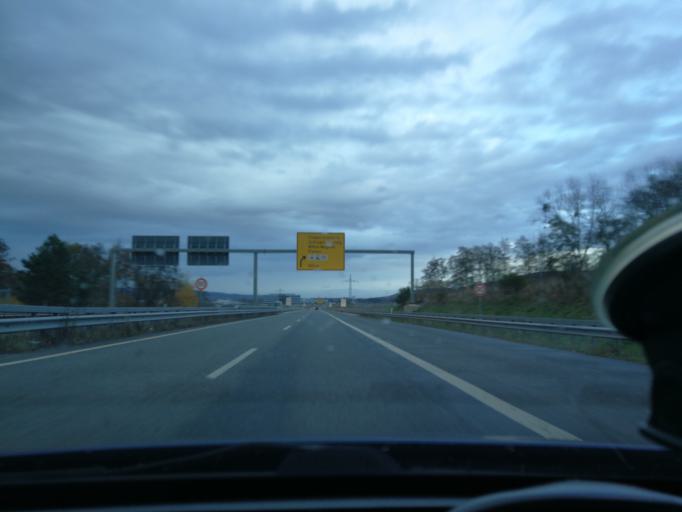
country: DE
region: Rheinland-Pfalz
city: Altrich
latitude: 49.9552
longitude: 6.9319
